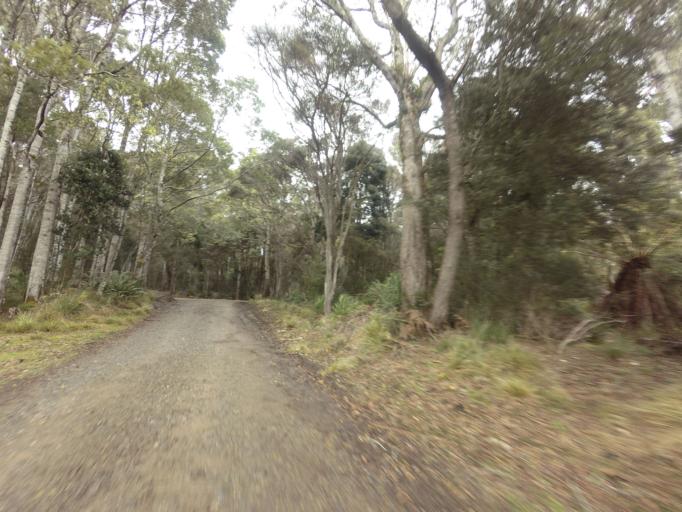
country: AU
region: Tasmania
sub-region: Huon Valley
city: Geeveston
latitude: -43.5550
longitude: 146.8872
